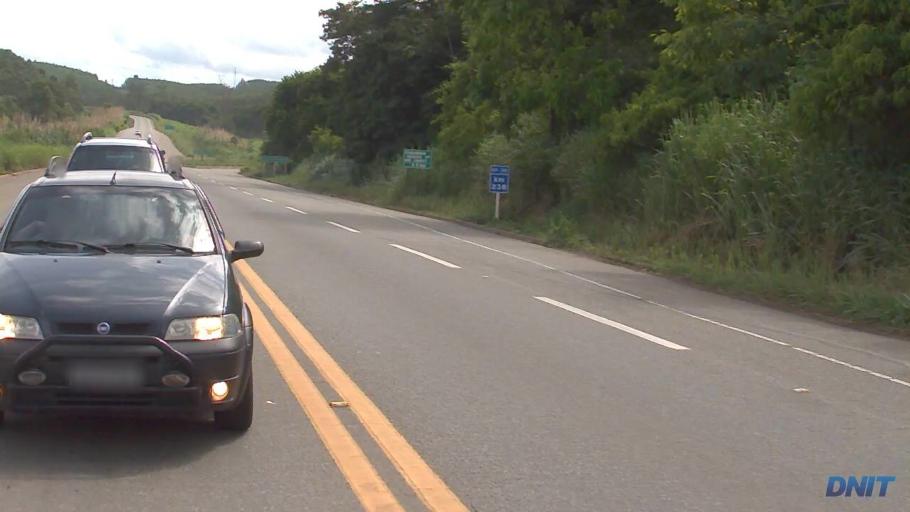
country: BR
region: Minas Gerais
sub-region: Ipaba
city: Ipaba
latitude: -19.3759
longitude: -42.4618
